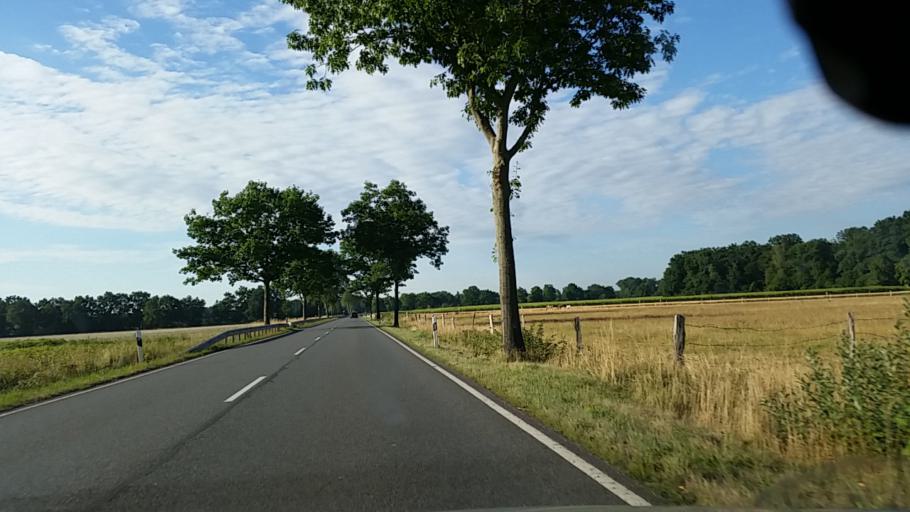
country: DE
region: Lower Saxony
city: Barwedel
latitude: 52.5636
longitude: 10.7881
